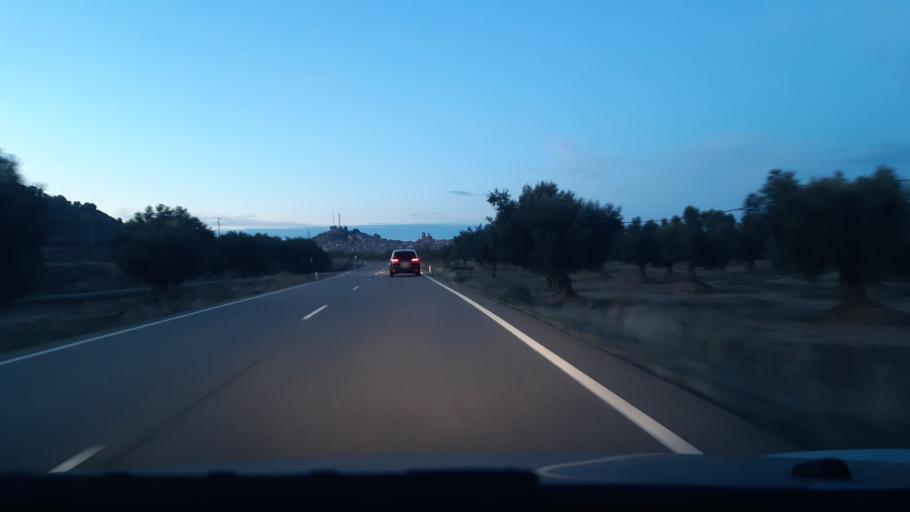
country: ES
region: Aragon
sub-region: Provincia de Teruel
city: Calaceite
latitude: 41.0054
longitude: 0.1924
